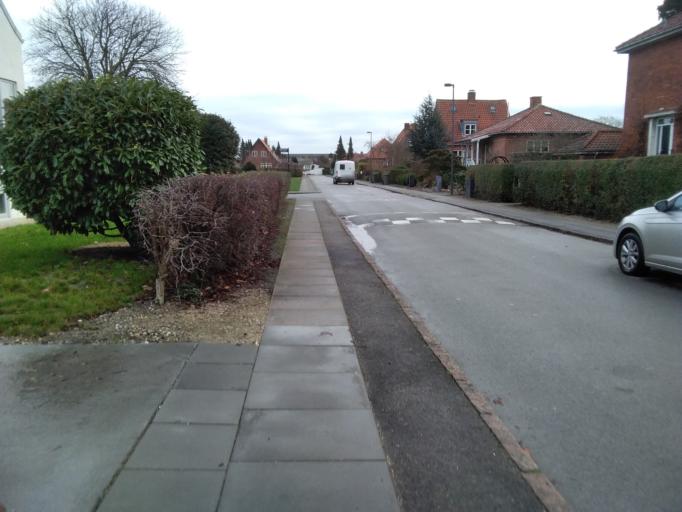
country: DK
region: Capital Region
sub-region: Tarnby Kommune
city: Tarnby
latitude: 55.6413
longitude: 12.6249
